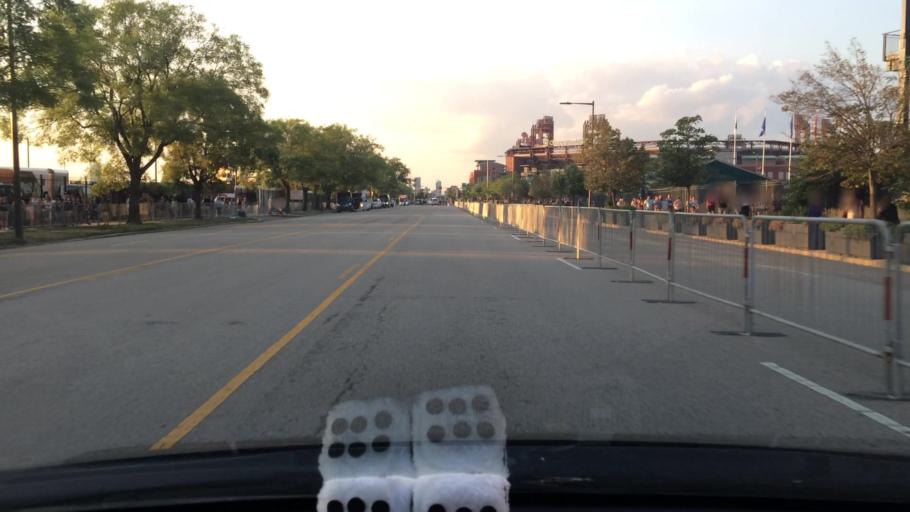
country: US
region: New Jersey
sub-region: Gloucester County
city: National Park
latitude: 39.9011
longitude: -75.1693
